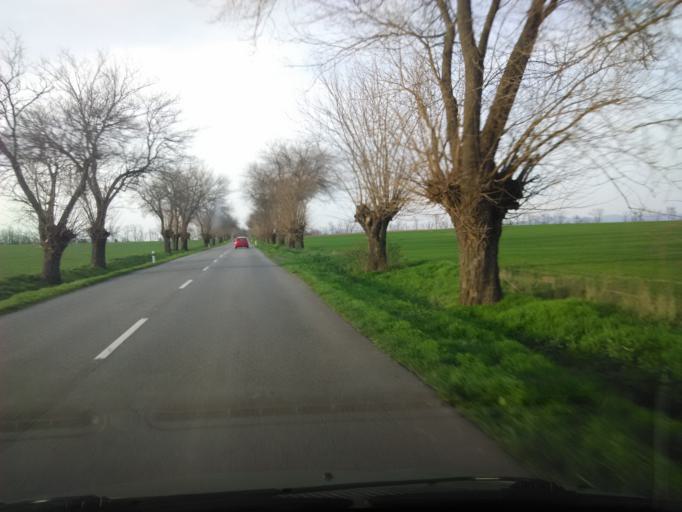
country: SK
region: Nitriansky
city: Tlmace
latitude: 48.1728
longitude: 18.4520
